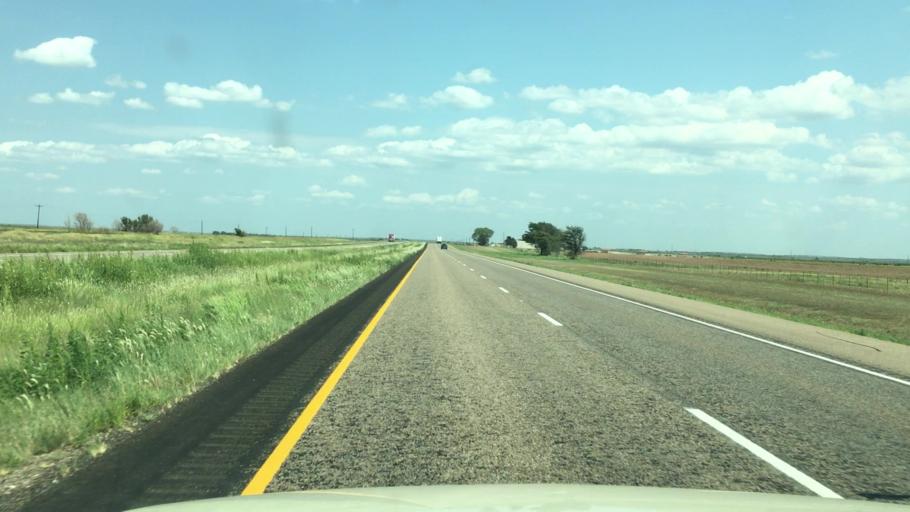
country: US
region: Texas
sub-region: Armstrong County
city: Claude
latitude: 35.0317
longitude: -101.1233
